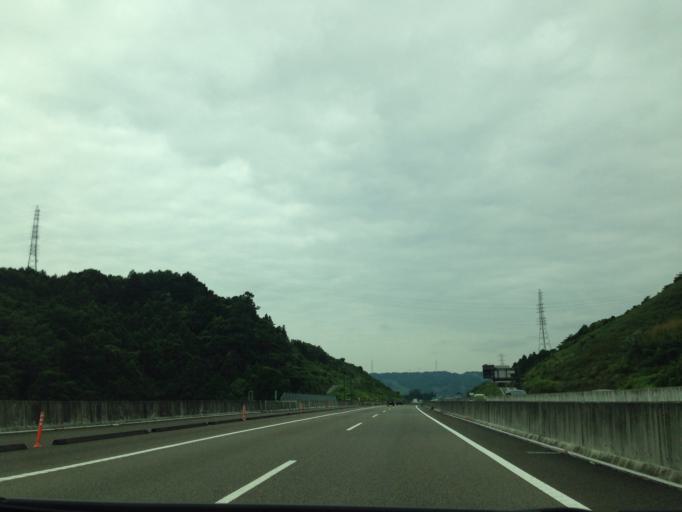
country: JP
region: Shizuoka
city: Kanaya
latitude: 34.8589
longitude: 138.1449
